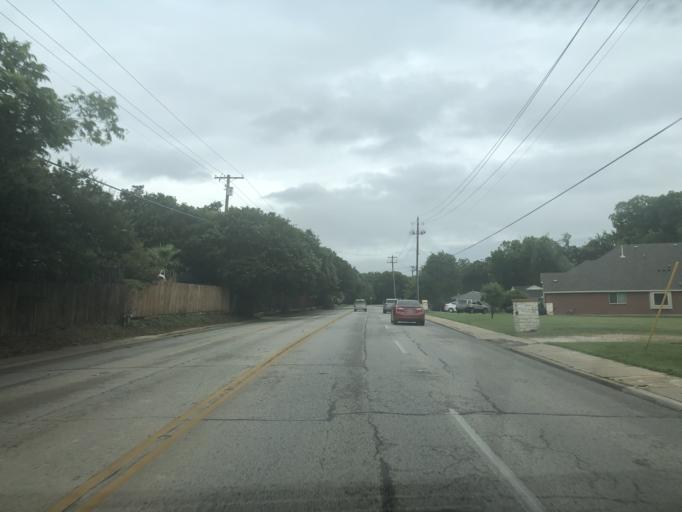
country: US
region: Texas
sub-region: Dallas County
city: Irving
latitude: 32.8013
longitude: -96.9707
